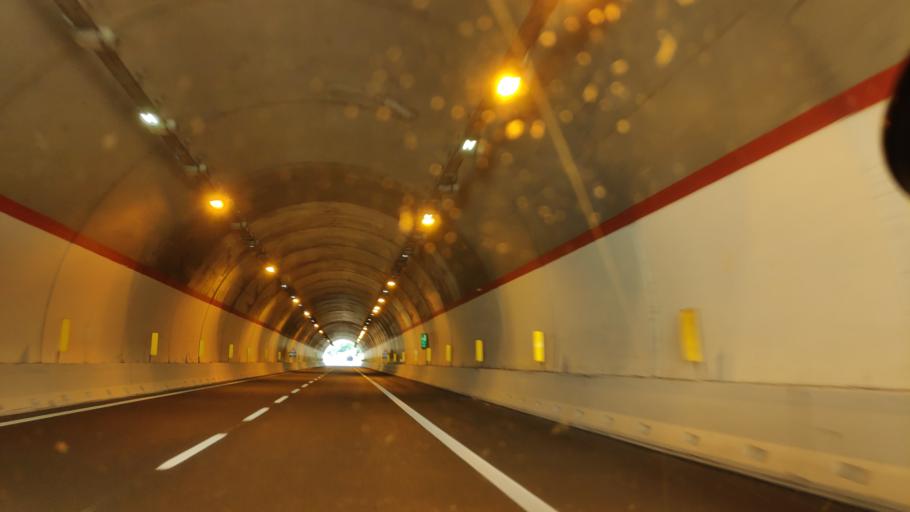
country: IT
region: Campania
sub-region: Provincia di Salerno
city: Casalbuono
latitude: 40.2333
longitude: 15.6647
